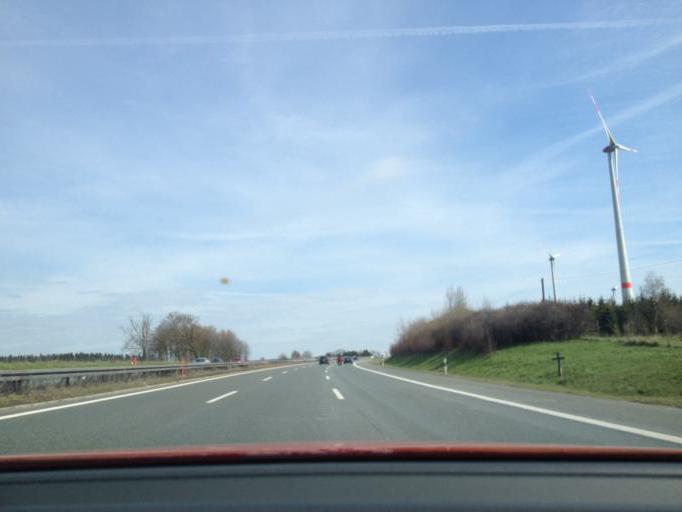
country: DE
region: Bavaria
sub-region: Upper Franconia
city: Gefrees
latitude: 50.1398
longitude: 11.7424
